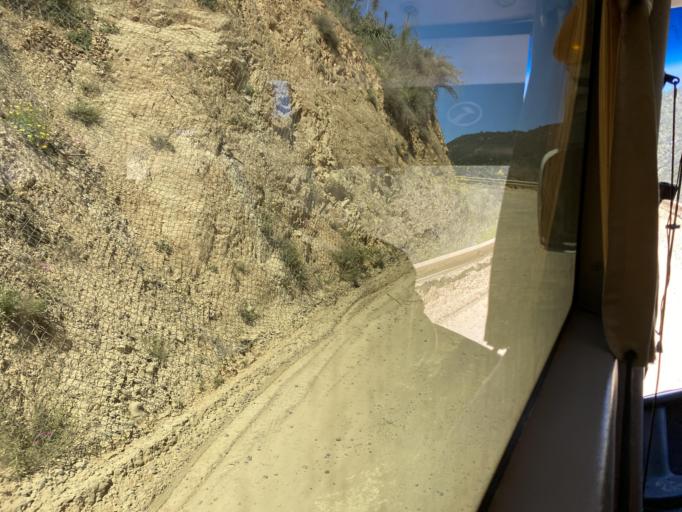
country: CL
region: Valparaiso
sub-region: Provincia de Marga Marga
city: Limache
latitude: -33.1992
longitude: -71.2642
